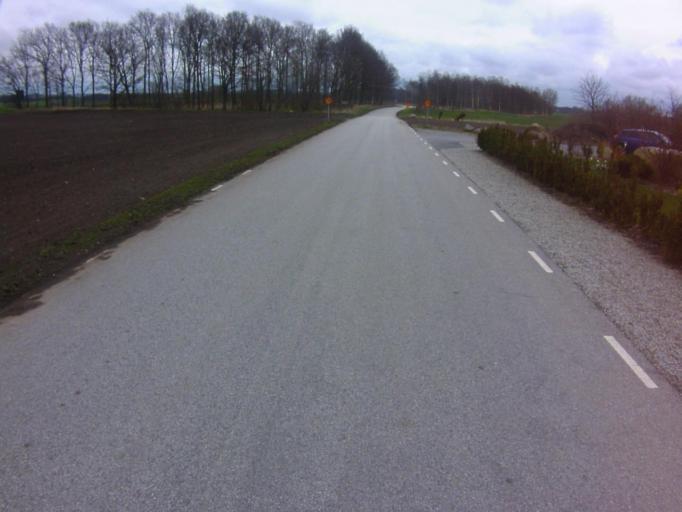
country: SE
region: Skane
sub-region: Lunds Kommun
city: Lund
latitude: 55.7916
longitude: 13.2152
